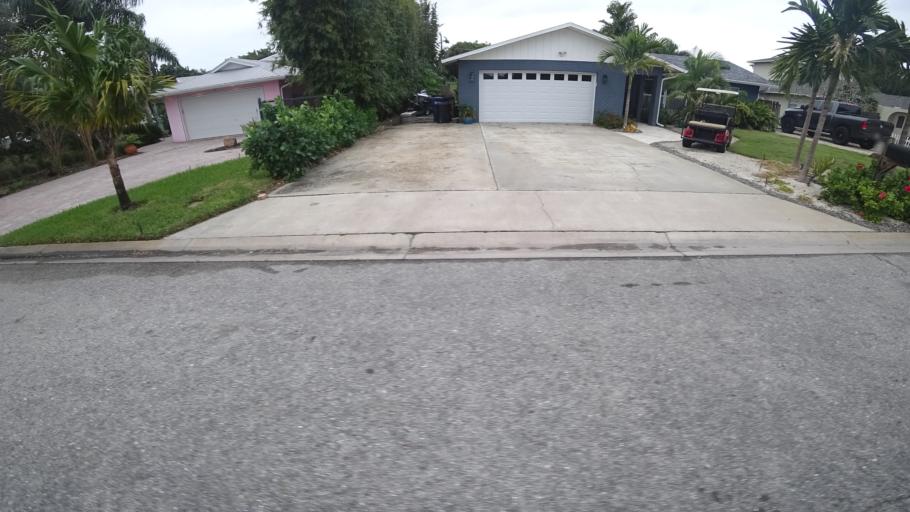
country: US
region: Florida
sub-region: Manatee County
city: West Bradenton
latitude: 27.5167
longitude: -82.6436
